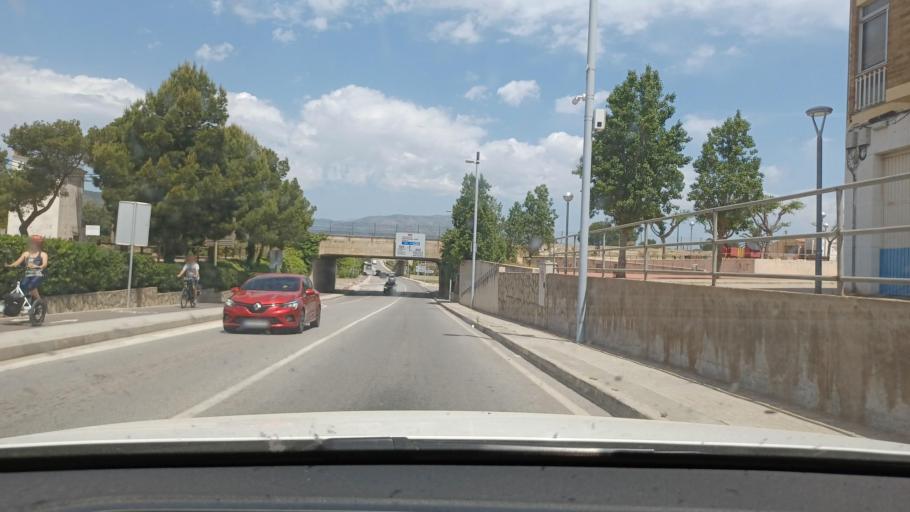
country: ES
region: Catalonia
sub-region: Provincia de Tarragona
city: Colldejou
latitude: 40.9949
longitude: 0.9202
